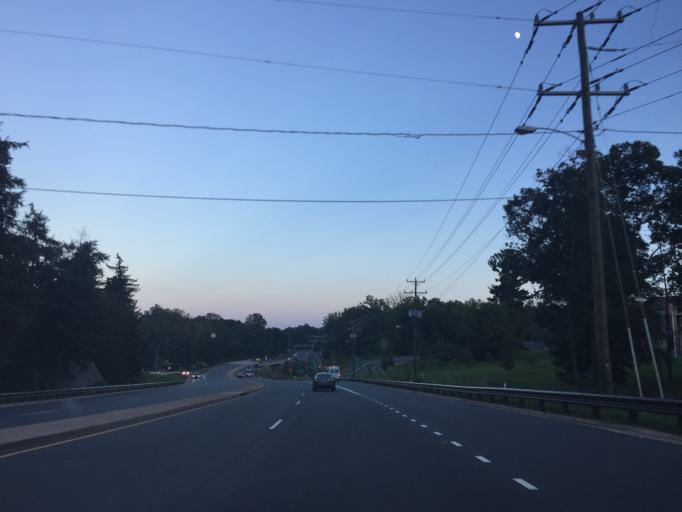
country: US
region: Virginia
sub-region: City of Charlottesville
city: Charlottesville
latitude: 38.0446
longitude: -78.4780
